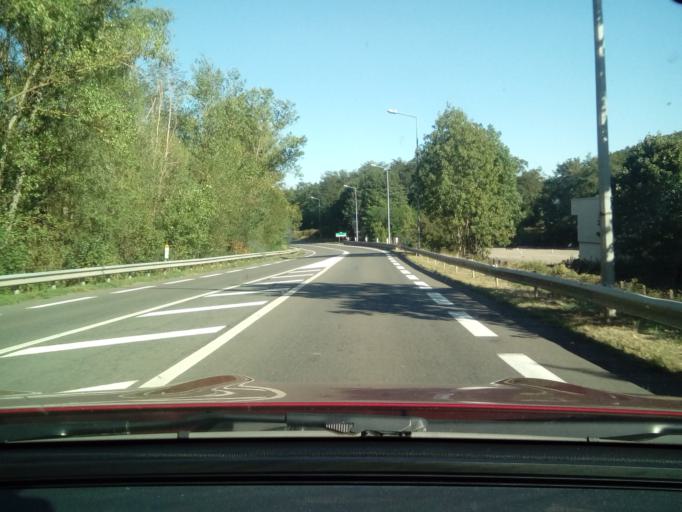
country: FR
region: Rhone-Alpes
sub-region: Departement du Rhone
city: Chatillon
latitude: 45.8895
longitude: 4.6079
